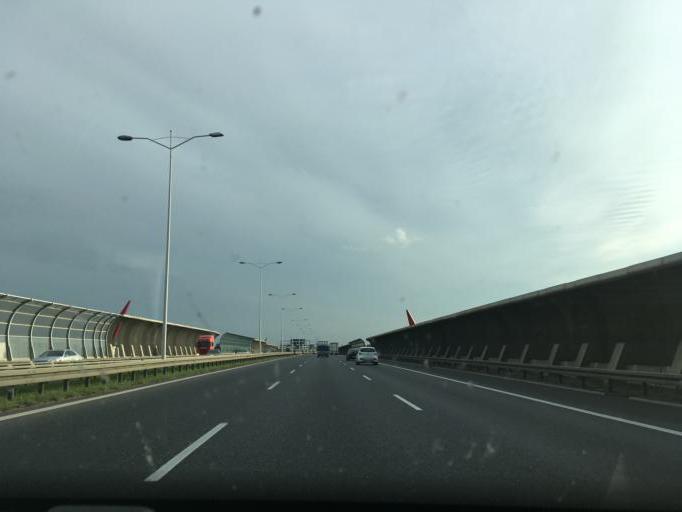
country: PL
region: Lower Silesian Voivodeship
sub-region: Powiat wroclawski
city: Smolec
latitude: 51.0965
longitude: 16.9323
